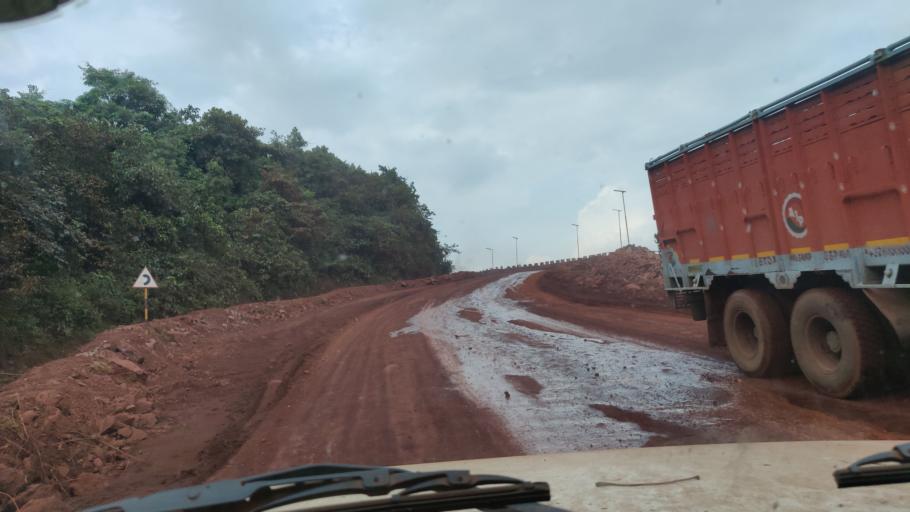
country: IN
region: Odisha
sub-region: Kendujhar
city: Barbil
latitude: 21.6260
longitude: 85.5129
